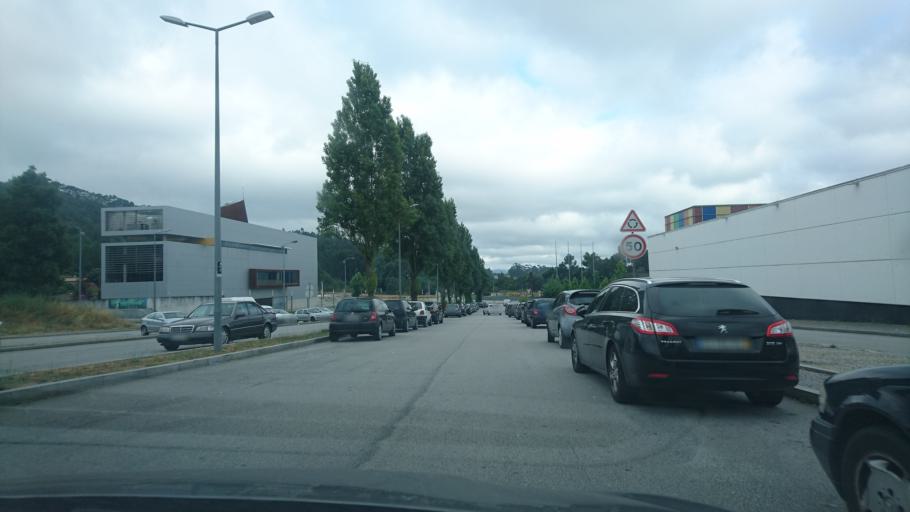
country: PT
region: Porto
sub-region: Valongo
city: Valongo
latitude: 41.1985
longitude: -8.4909
